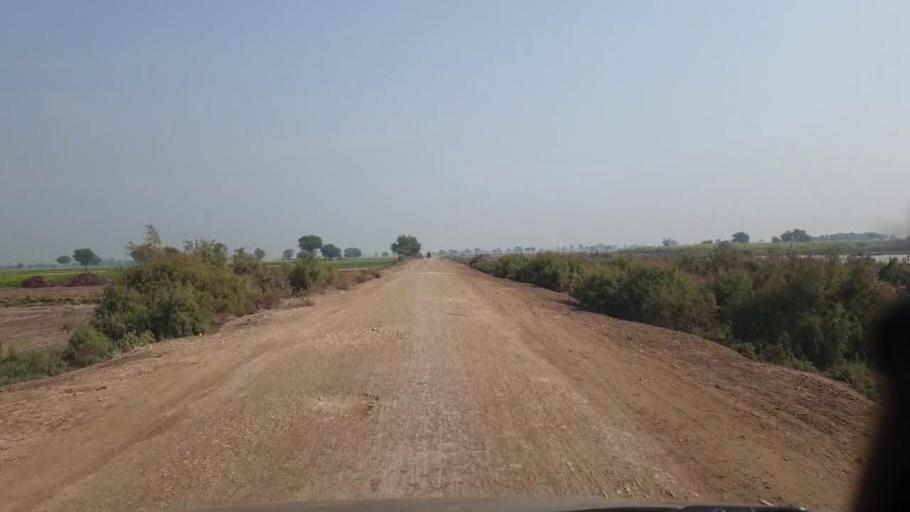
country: PK
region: Sindh
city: Shahdadpur
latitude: 26.0413
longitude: 68.4865
